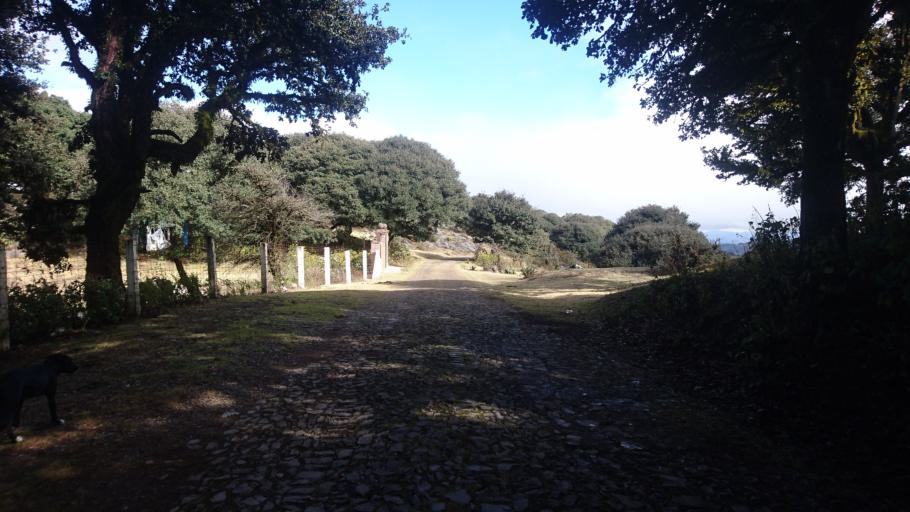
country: MX
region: San Luis Potosi
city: Zaragoza
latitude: 22.0679
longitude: -100.6459
